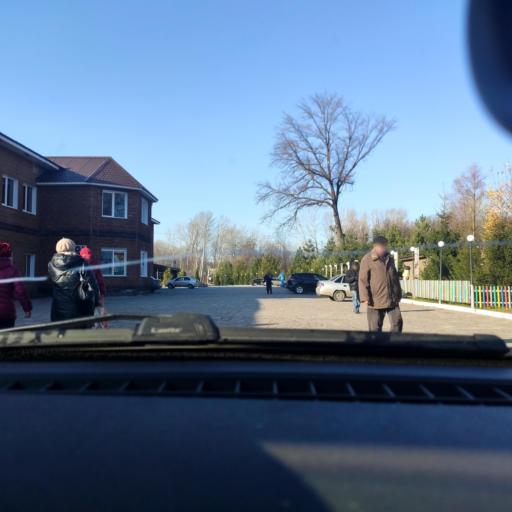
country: RU
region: Bashkortostan
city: Ufa
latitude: 54.7857
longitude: 56.1019
